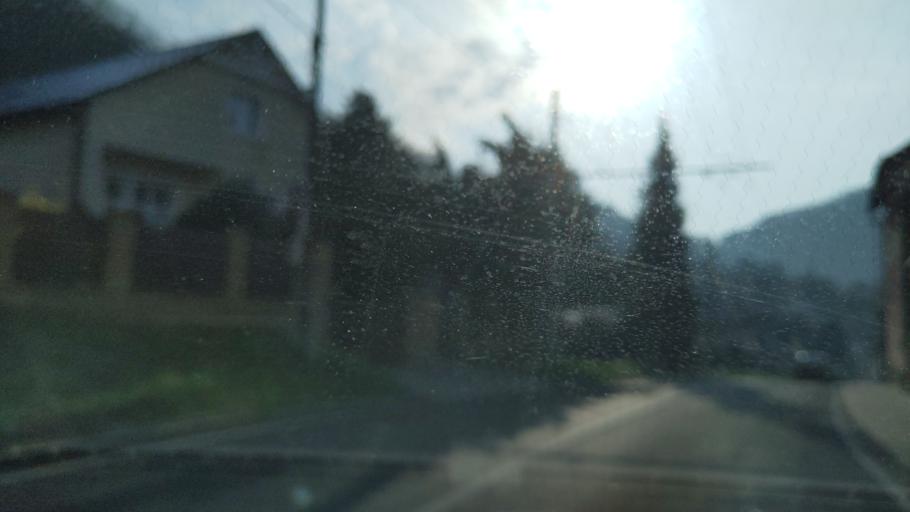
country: CZ
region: Ustecky
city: Velke Brezno
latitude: 50.6817
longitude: 14.1194
